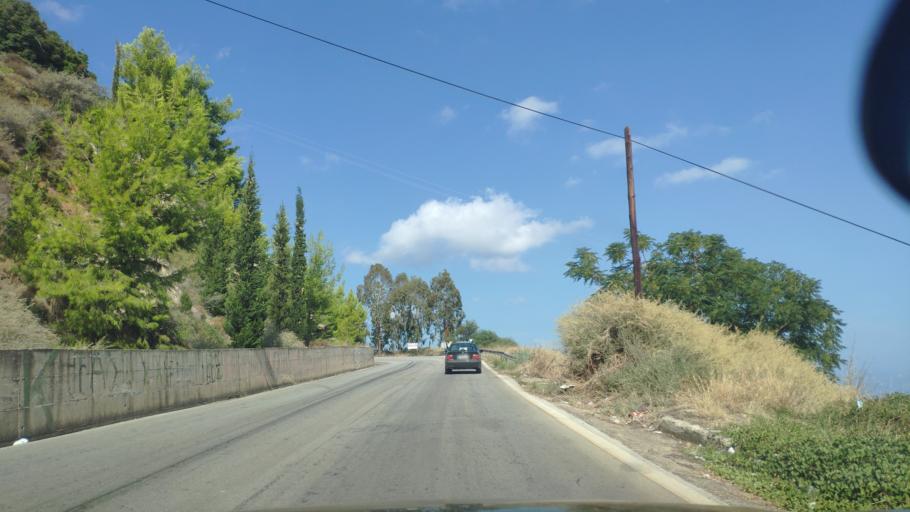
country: GR
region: Peloponnese
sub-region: Nomos Korinthias
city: Moulki
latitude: 37.9990
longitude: 22.7145
